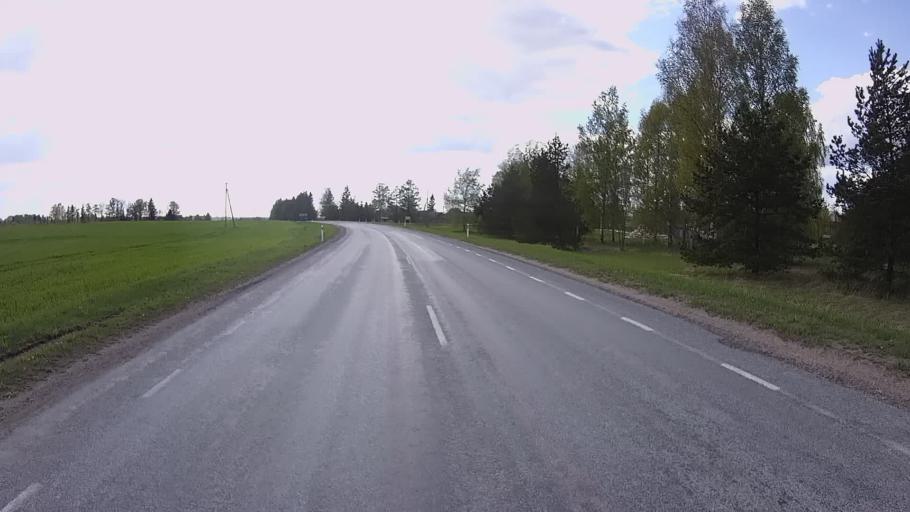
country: EE
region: Tartu
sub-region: Tartu linn
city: Tartu
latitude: 58.5099
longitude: 26.8929
